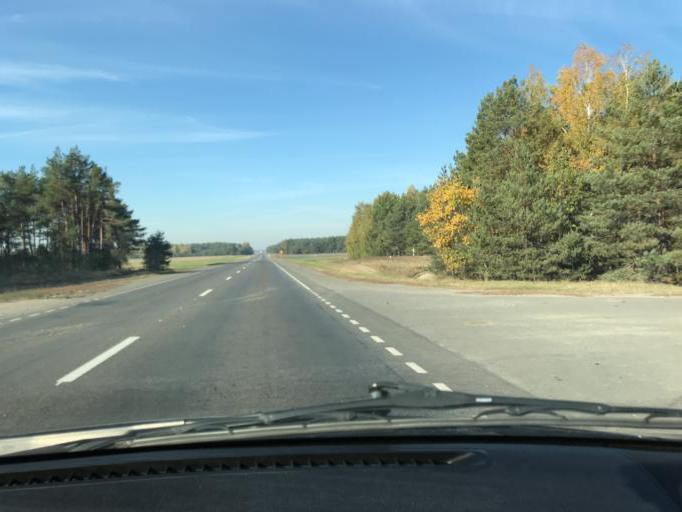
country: BY
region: Brest
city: Davyd-Haradok
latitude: 52.2368
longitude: 27.2298
